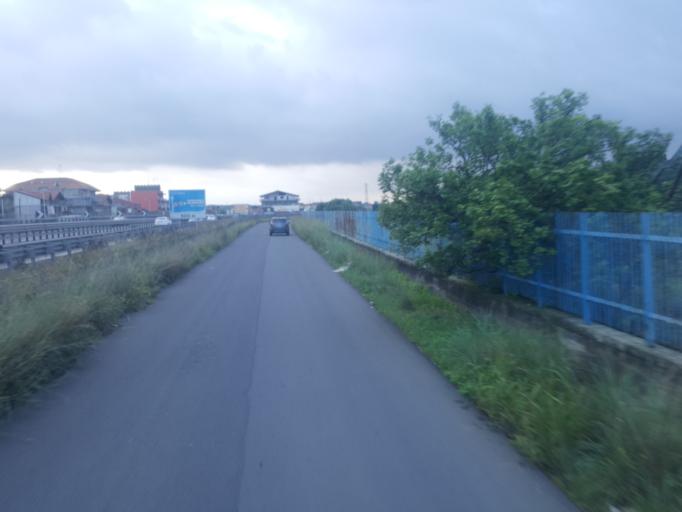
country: IT
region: Sicily
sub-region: Catania
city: Belvedere-Piano Tavola
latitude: 37.5367
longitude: 14.9774
